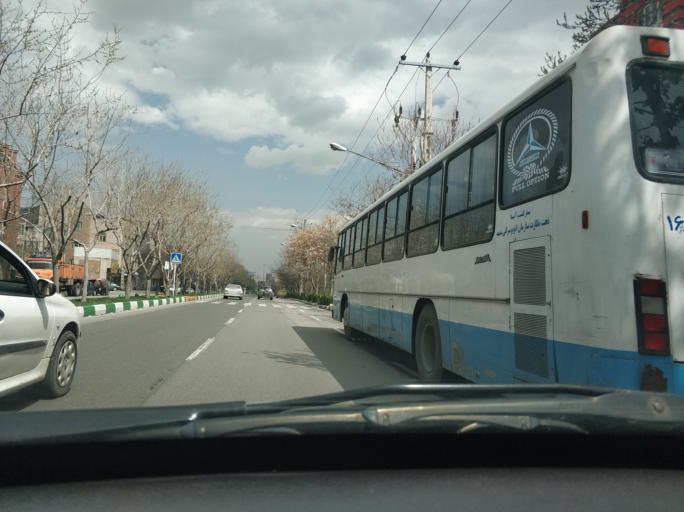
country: IR
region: Razavi Khorasan
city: Mashhad
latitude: 36.2810
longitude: 59.5774
